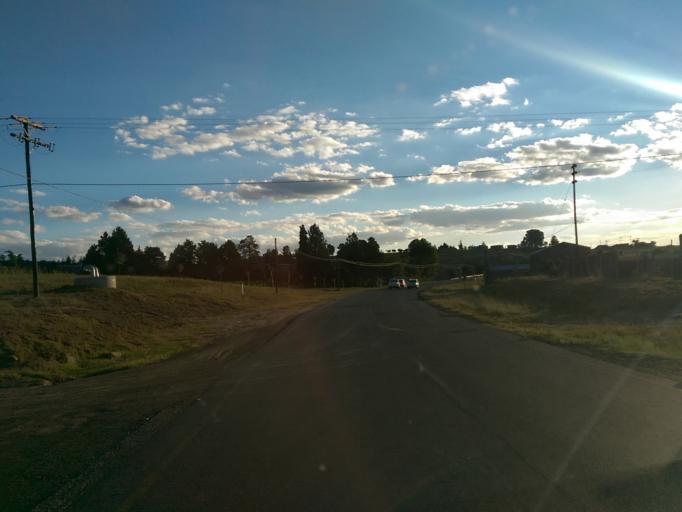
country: LS
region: Maseru
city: Maseru
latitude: -29.3488
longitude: 27.6619
